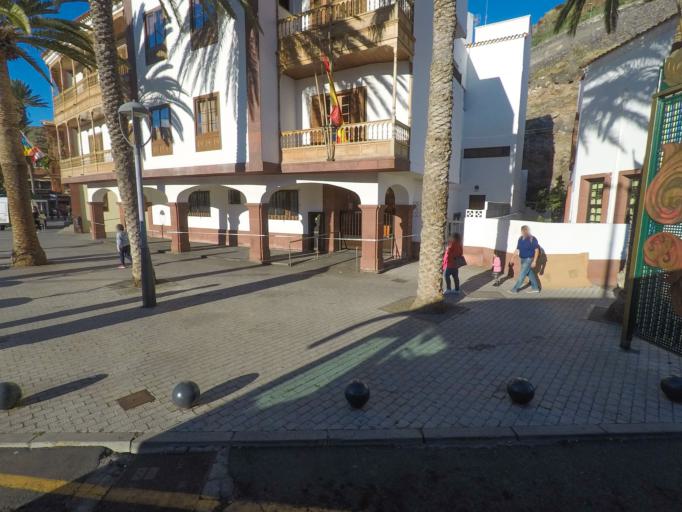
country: ES
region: Canary Islands
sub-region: Provincia de Santa Cruz de Tenerife
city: San Sebastian de la Gomera
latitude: 28.0902
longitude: -17.1096
